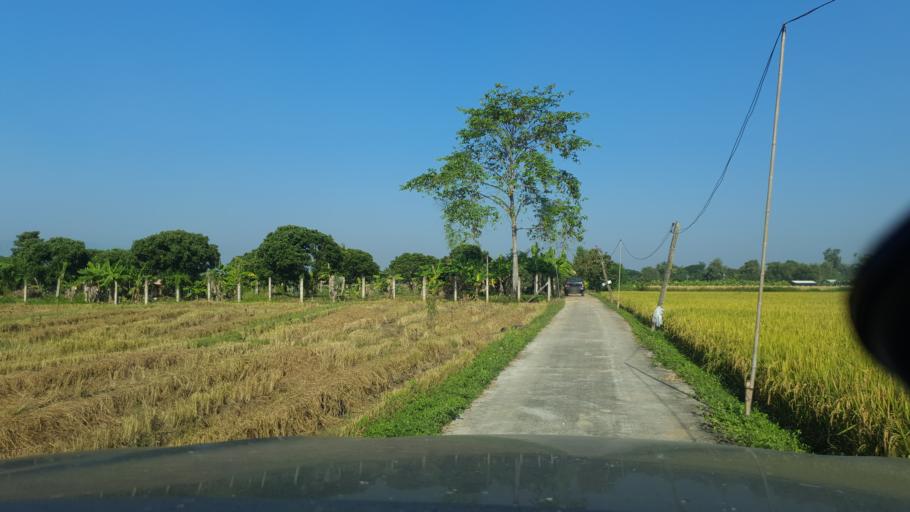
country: TH
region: Chiang Mai
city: San Kamphaeng
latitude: 18.7604
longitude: 99.1343
